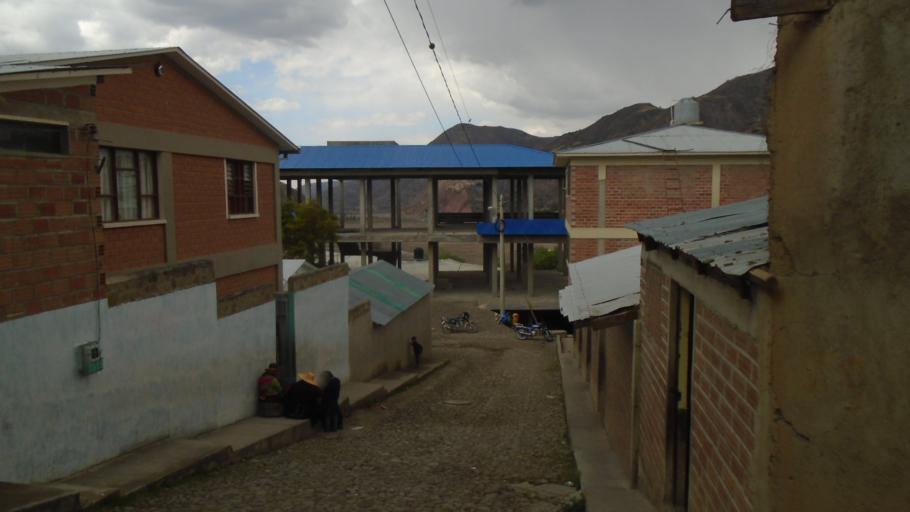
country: BO
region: Cochabamba
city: Colchani
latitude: -17.5165
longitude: -66.6190
